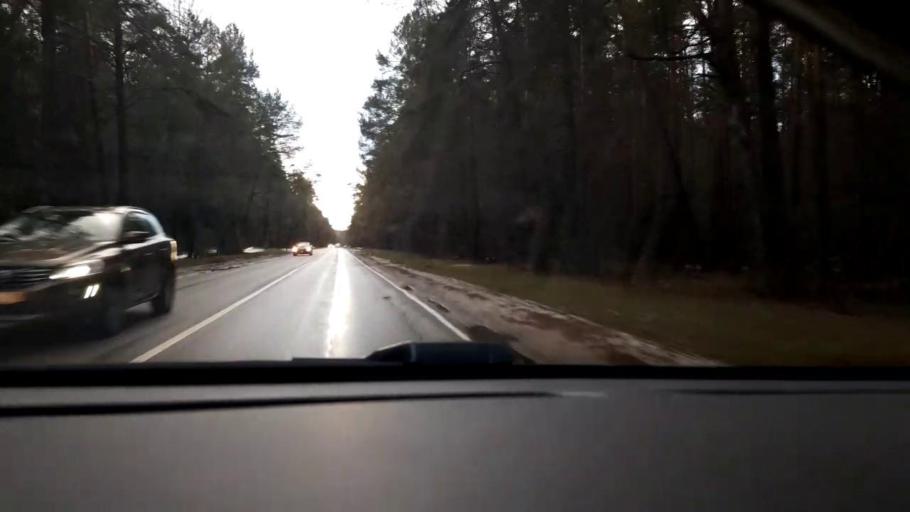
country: LT
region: Vilnius County
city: Rasos
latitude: 54.7707
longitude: 25.3809
